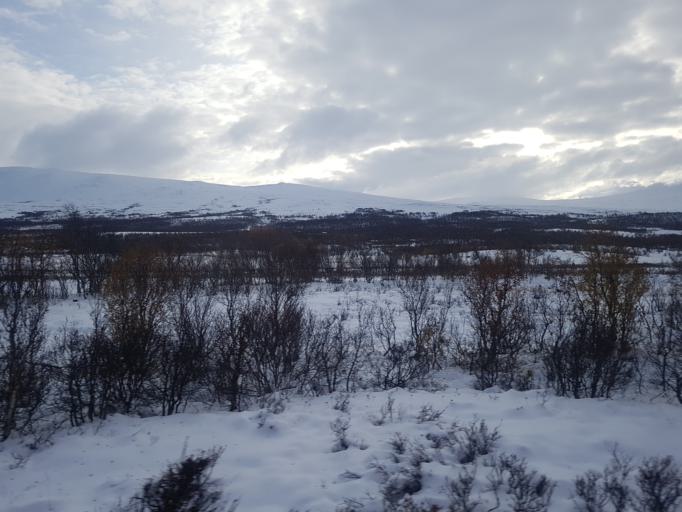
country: NO
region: Oppland
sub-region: Dovre
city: Dovre
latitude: 62.1208
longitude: 9.2944
